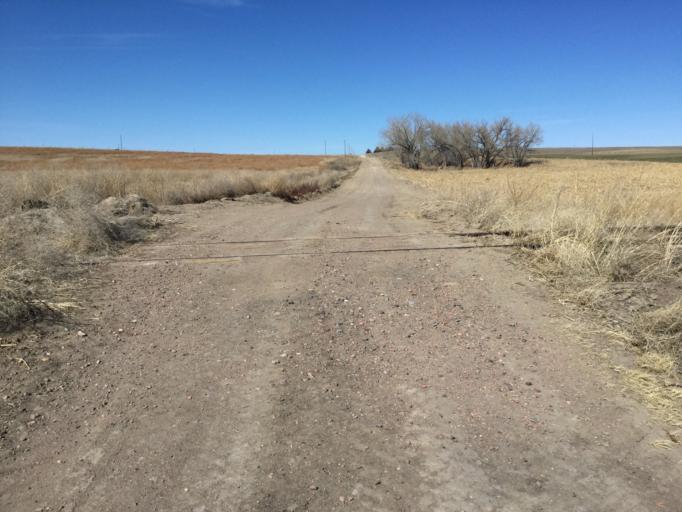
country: US
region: Kansas
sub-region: Decatur County
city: Oberlin
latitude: 39.9088
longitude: -100.7587
